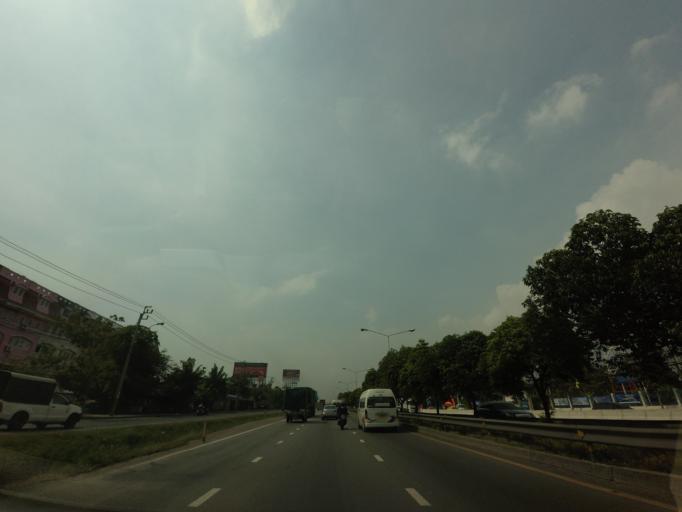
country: TH
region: Bangkok
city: Thawi Watthana
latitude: 13.7877
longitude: 100.3626
